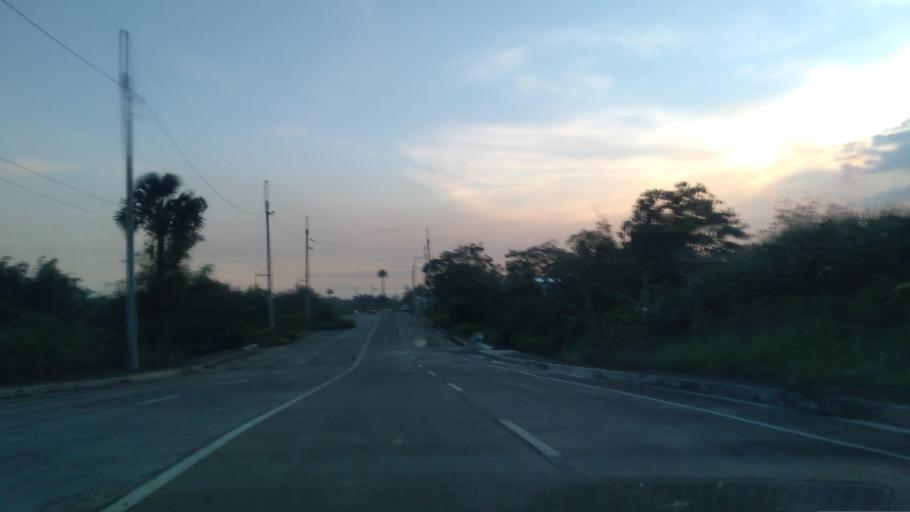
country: PH
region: Calabarzon
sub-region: Province of Quezon
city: Isabang
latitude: 13.9646
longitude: 121.5779
